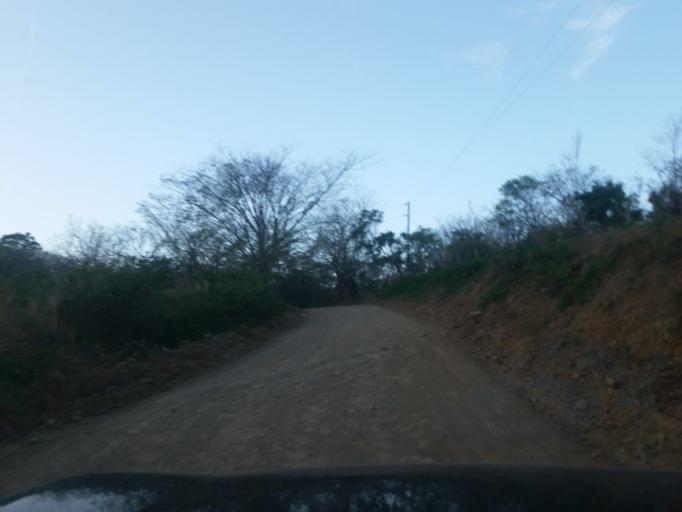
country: NI
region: Rivas
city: San Juan del Sur
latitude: 11.2133
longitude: -85.8099
